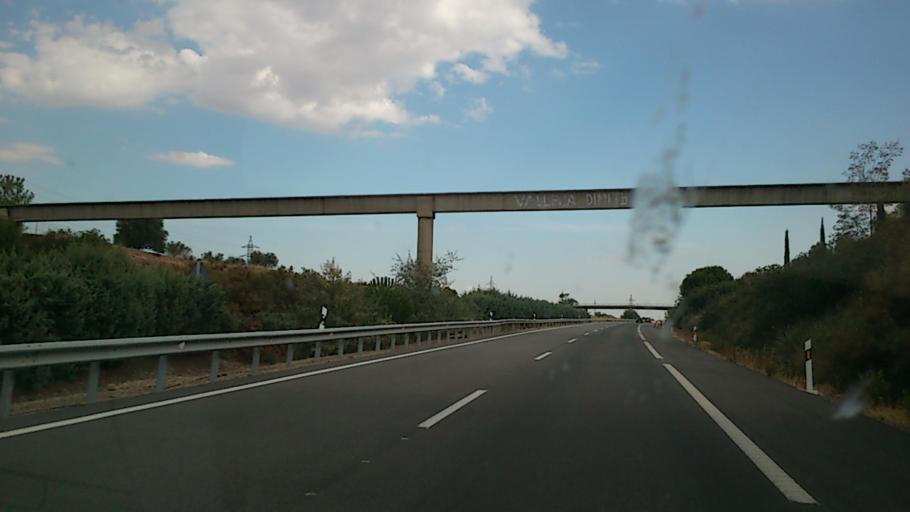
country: ES
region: La Rioja
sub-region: Provincia de La Rioja
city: Calahorra
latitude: 42.2856
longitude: -1.9491
